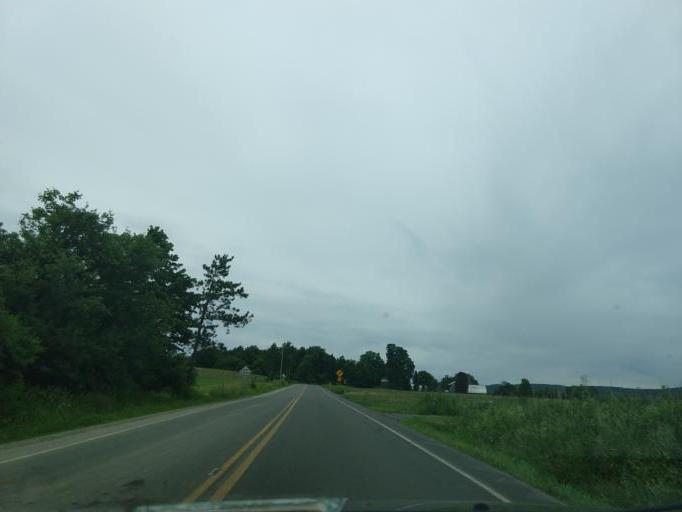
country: US
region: New York
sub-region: Tompkins County
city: Dryden
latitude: 42.4888
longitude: -76.2435
